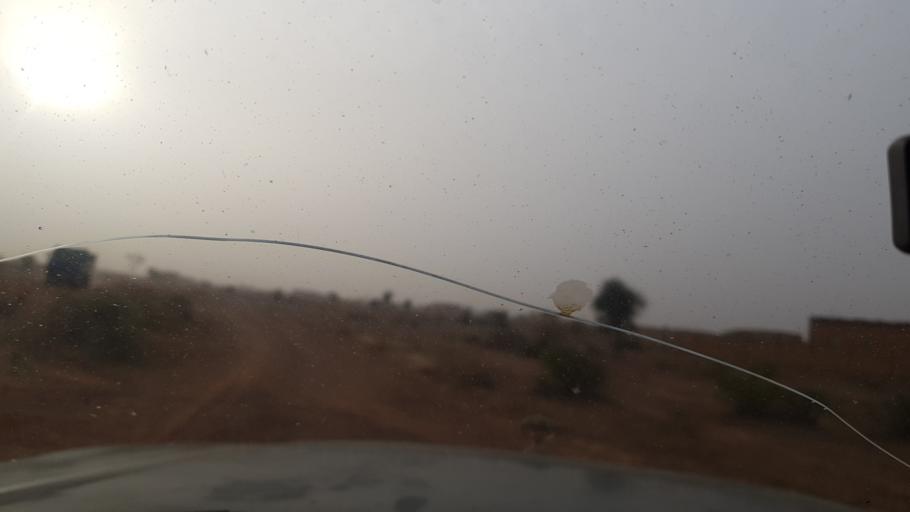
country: NE
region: Niamey
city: Niamey
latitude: 13.4908
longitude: 2.2178
